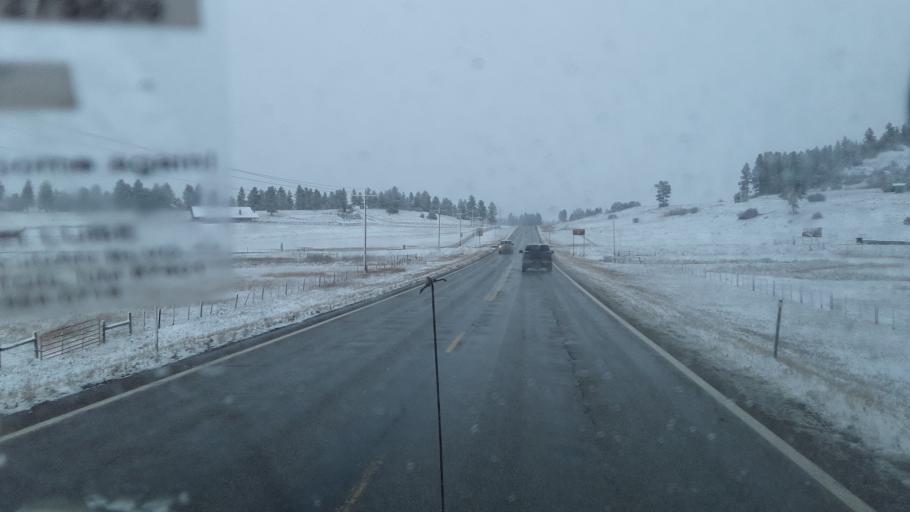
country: US
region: Colorado
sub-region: Archuleta County
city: Pagosa Springs
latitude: 37.2174
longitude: -106.9846
